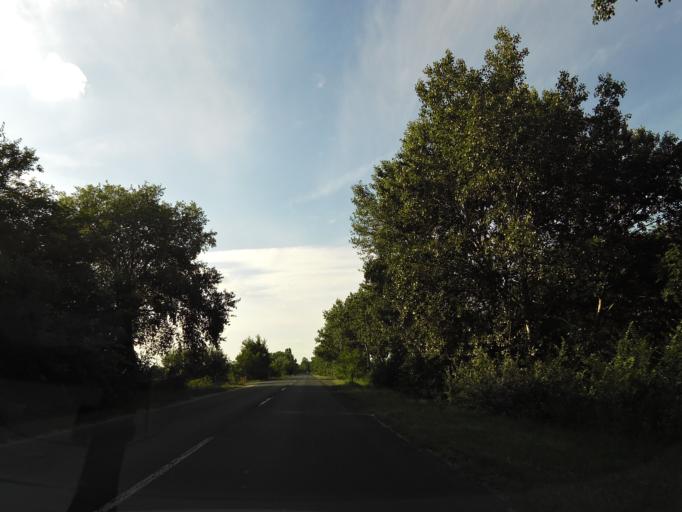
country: HU
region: Csongrad
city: Szatymaz
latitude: 46.3695
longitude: 20.0443
